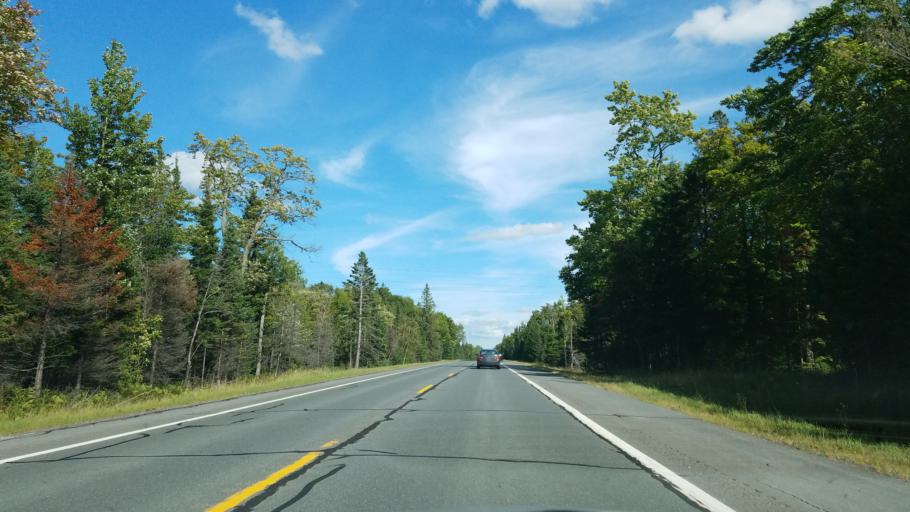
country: US
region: Michigan
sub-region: Baraga County
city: L'Anse
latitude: 46.5788
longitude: -88.4254
